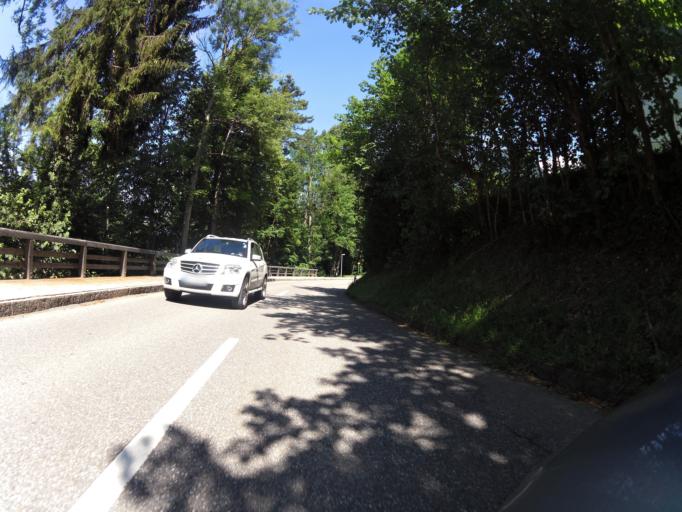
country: DE
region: Bavaria
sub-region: Upper Bavaria
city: Berchtesgaden
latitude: 47.6225
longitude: 12.9917
